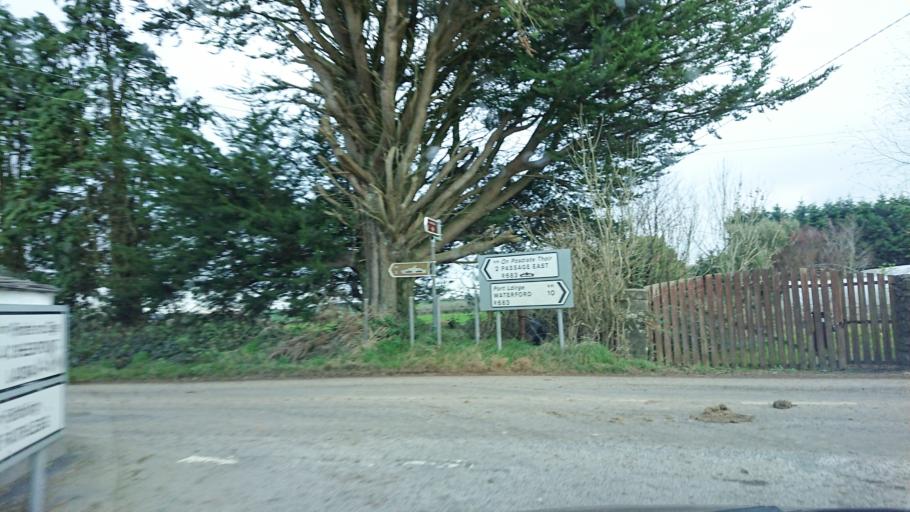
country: IE
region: Munster
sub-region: Waterford
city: Dunmore East
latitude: 52.2446
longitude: -6.9953
